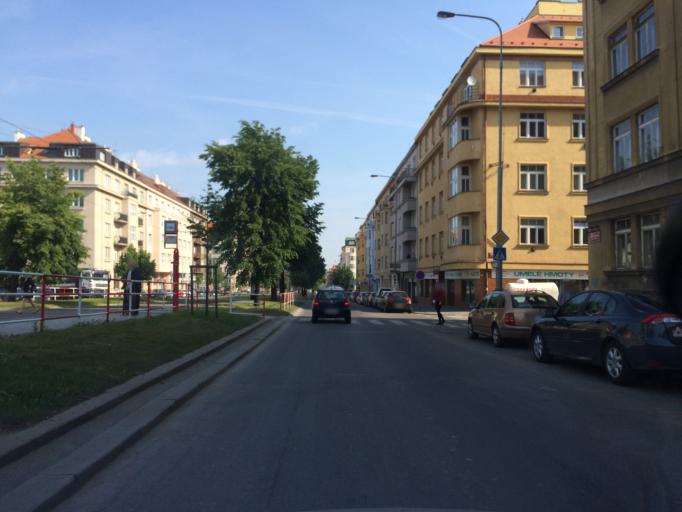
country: CZ
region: Praha
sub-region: Praha 1
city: Mala Strana
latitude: 50.1040
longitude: 14.3952
